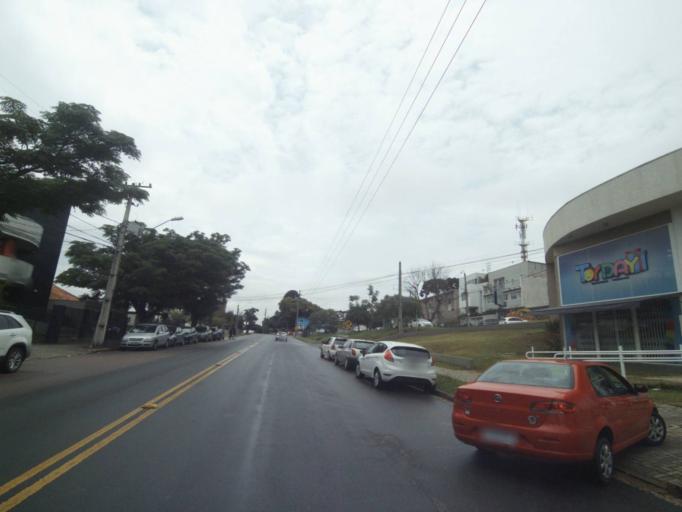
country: BR
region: Parana
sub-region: Curitiba
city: Curitiba
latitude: -25.4091
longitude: -49.2825
